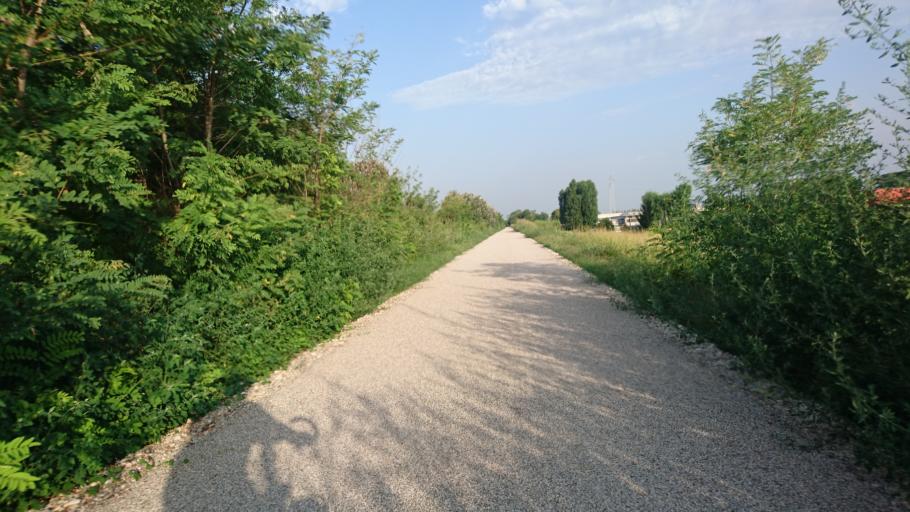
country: IT
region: Veneto
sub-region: Provincia di Padova
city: San Vito
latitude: 45.4202
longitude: 11.9767
